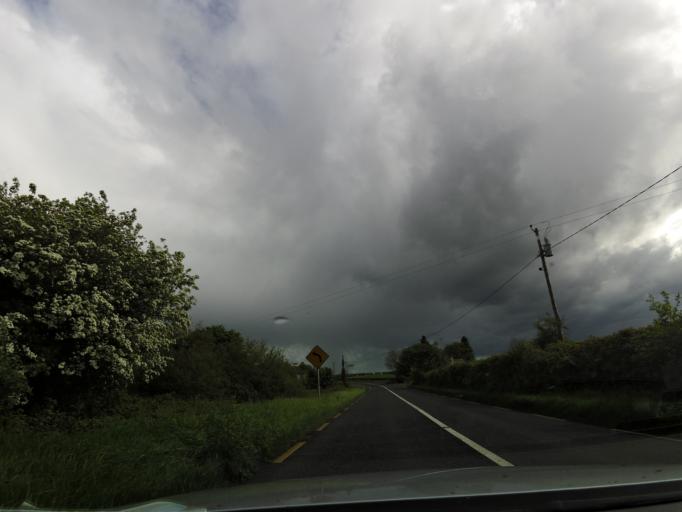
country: IE
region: Munster
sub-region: North Tipperary
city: Templemore
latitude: 52.7377
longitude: -7.8407
